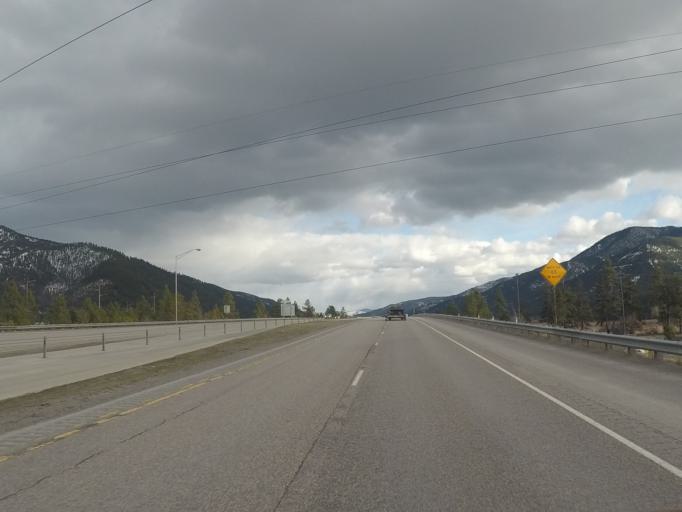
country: US
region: Montana
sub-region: Missoula County
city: Bonner-West Riverside
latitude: 46.8755
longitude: -113.8920
